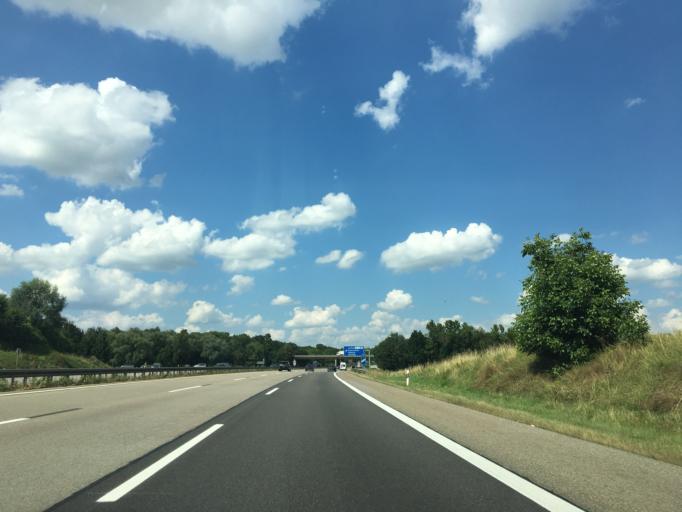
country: DE
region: Bavaria
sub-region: Upper Bavaria
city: Hepberg
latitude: 48.8125
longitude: 11.4664
